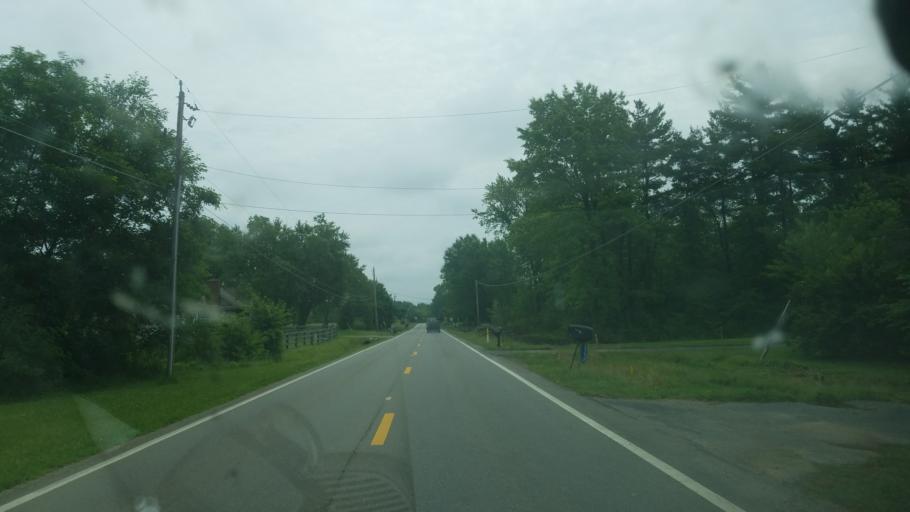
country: US
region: Ohio
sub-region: Franklin County
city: New Albany
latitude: 40.0186
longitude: -82.7750
